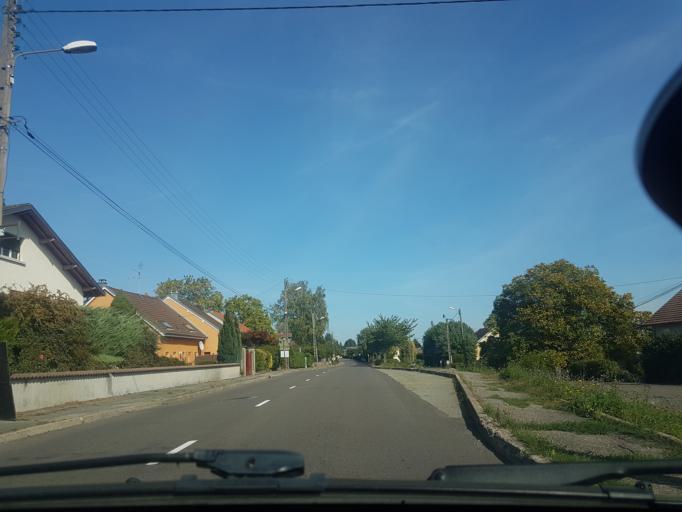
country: FR
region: Franche-Comte
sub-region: Territoire de Belfort
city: Offemont
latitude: 47.6652
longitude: 6.8854
